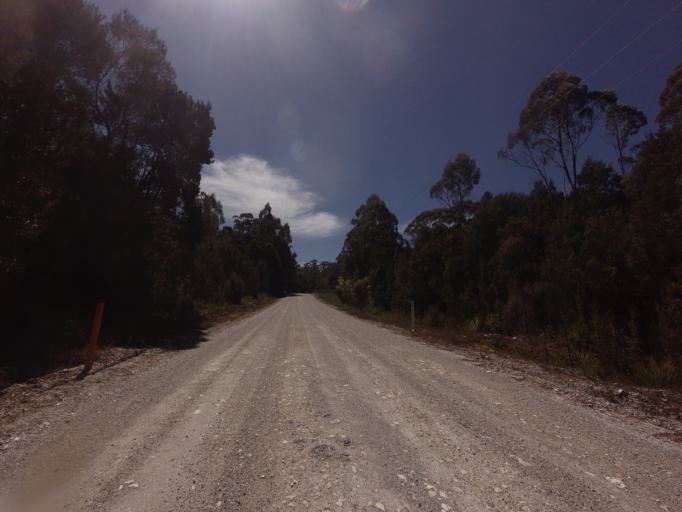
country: AU
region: Tasmania
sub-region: West Coast
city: Queenstown
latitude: -42.7568
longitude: 145.9859
